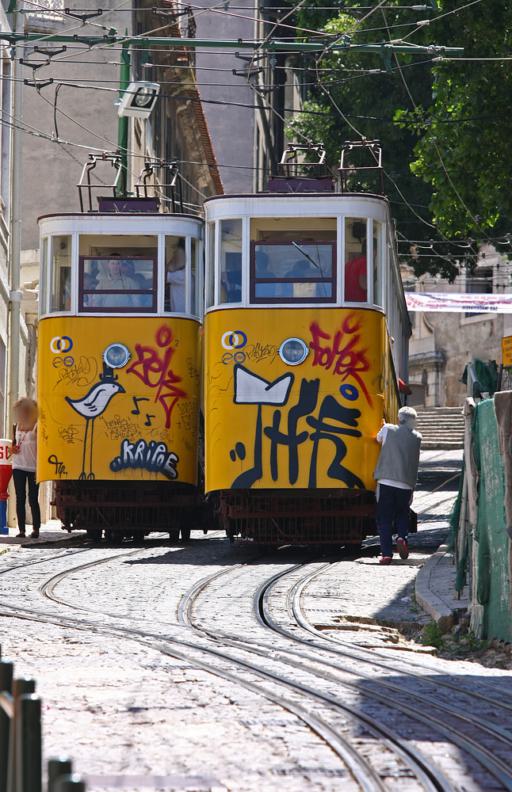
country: PT
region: Lisbon
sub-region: Lisbon
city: Lisbon
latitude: 38.7159
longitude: -9.1431
